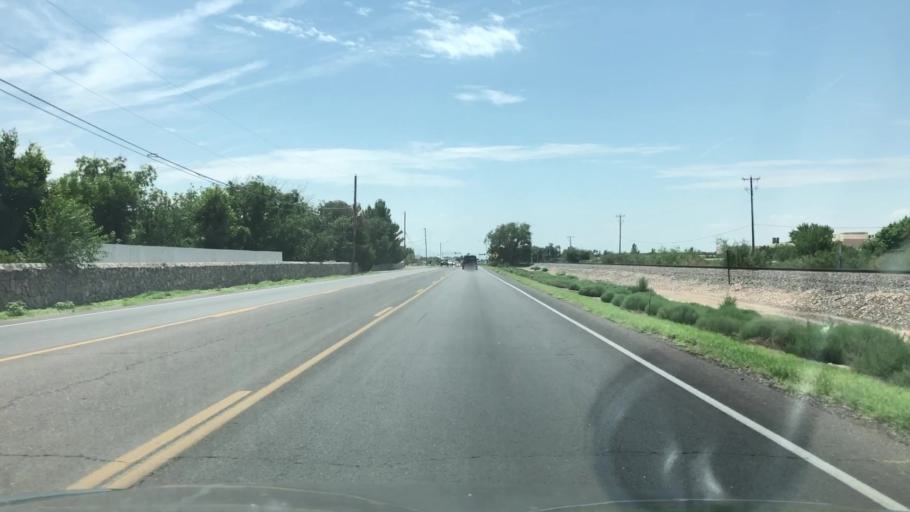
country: US
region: New Mexico
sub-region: Dona Ana County
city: University Park
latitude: 32.2647
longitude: -106.7599
